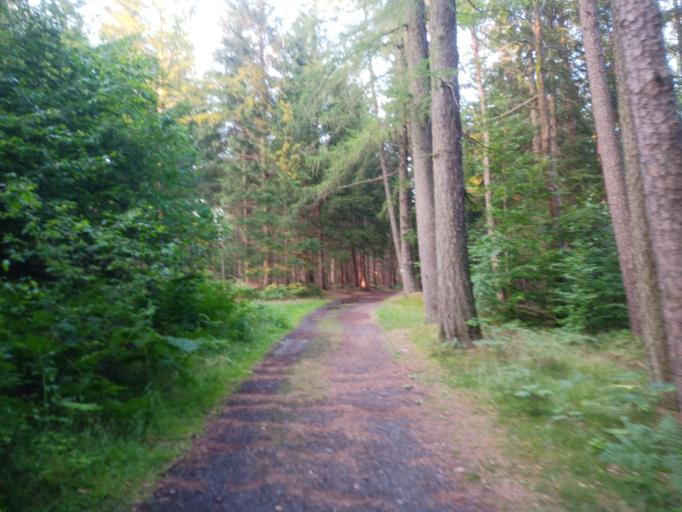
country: PL
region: Lower Silesian Voivodeship
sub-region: Powiat lubanski
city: Swieradow-Zdroj
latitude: 50.9187
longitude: 15.3338
